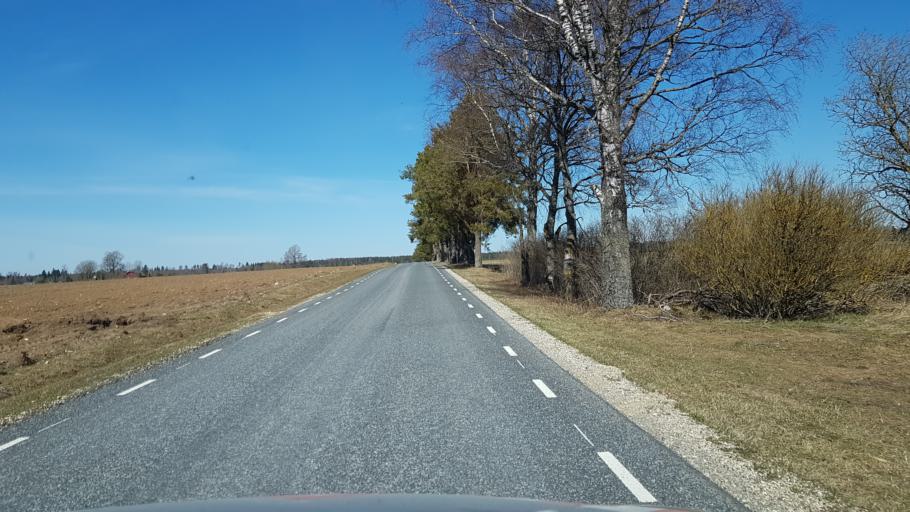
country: EE
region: Laeaene-Virumaa
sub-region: Vinni vald
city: Vinni
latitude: 59.1065
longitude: 26.5253
